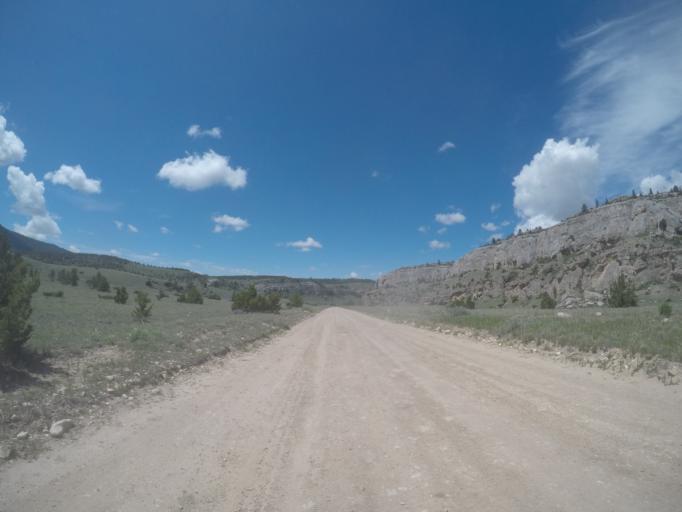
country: US
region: Wyoming
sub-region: Big Horn County
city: Lovell
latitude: 45.2230
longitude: -108.5861
